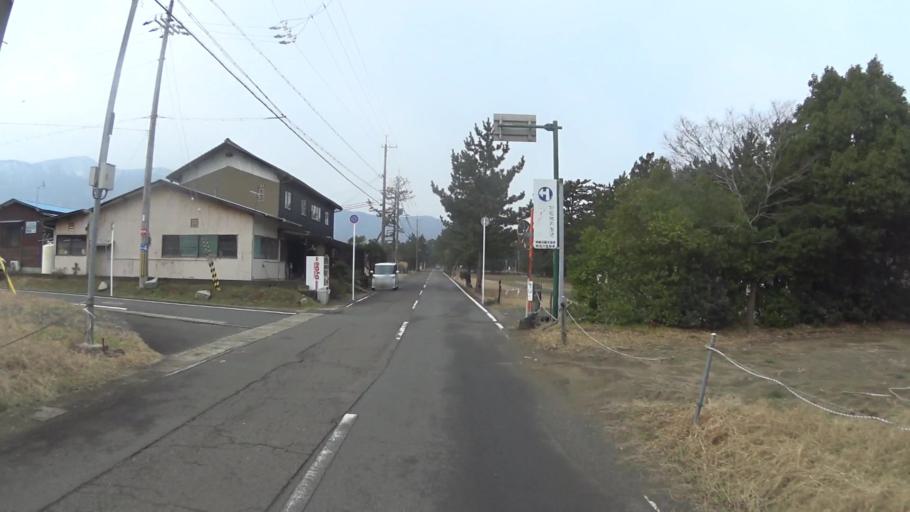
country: JP
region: Kyoto
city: Maizuru
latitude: 35.5133
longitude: 135.3004
